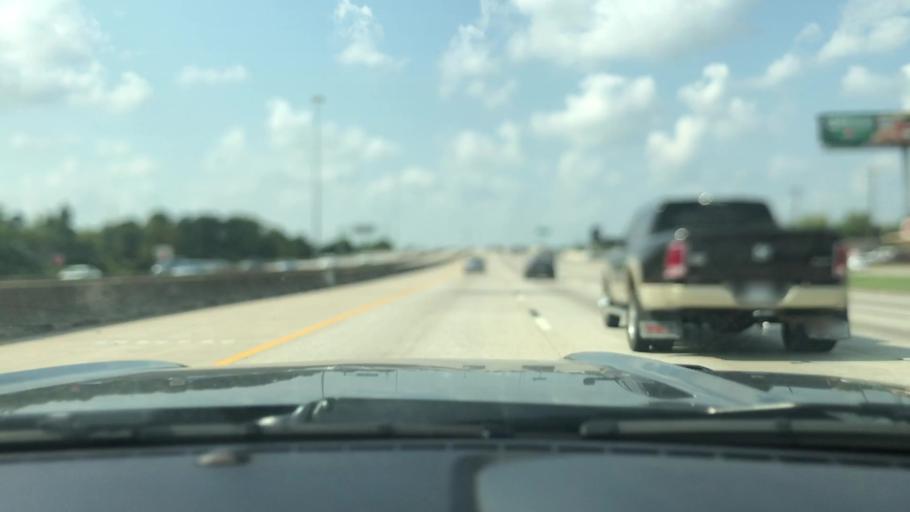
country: US
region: Texas
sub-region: Harris County
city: Aldine
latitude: 29.8835
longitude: -95.3221
